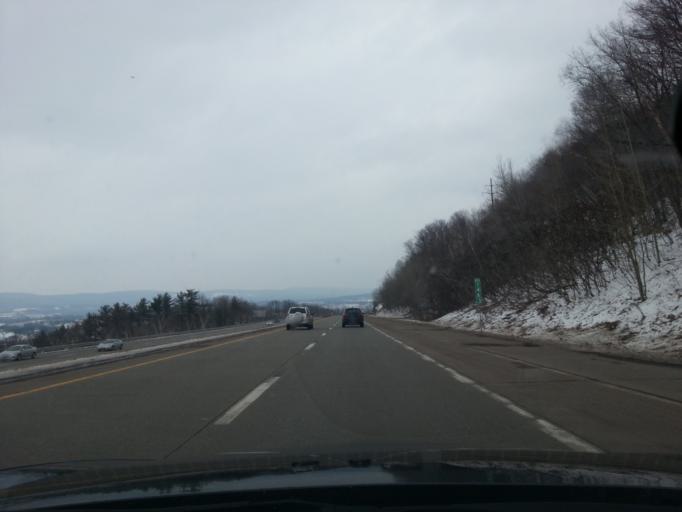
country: US
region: Pennsylvania
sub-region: Luzerne County
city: Conyngham
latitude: 40.9886
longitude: -76.0299
